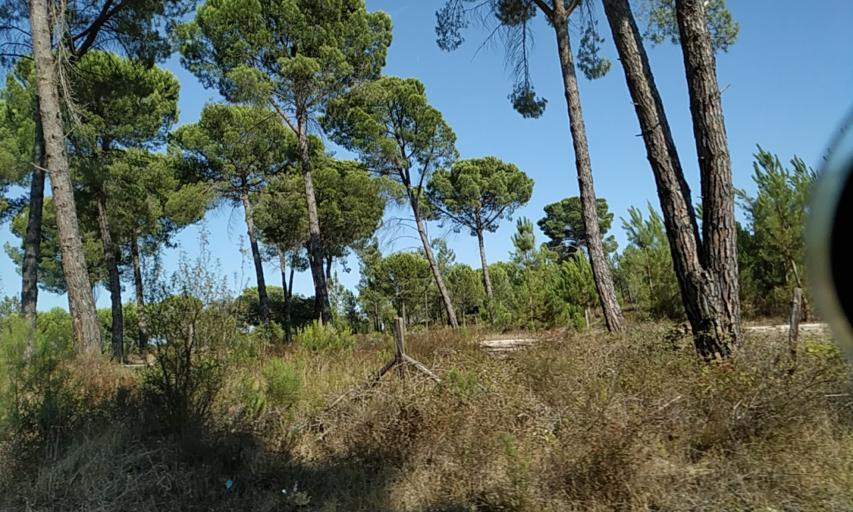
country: PT
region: Santarem
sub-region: Coruche
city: Coruche
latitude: 38.9002
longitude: -8.5312
